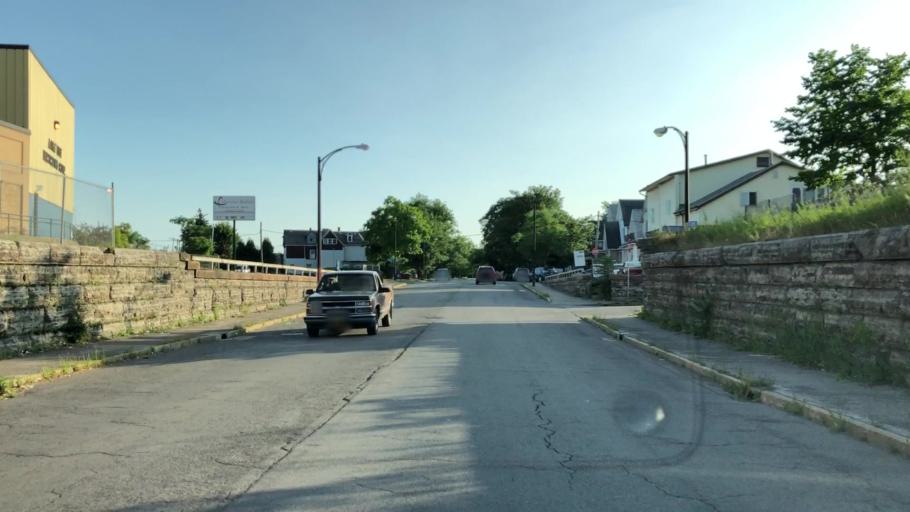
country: US
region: New York
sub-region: Erie County
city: Buffalo
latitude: 42.8770
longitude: -78.8416
